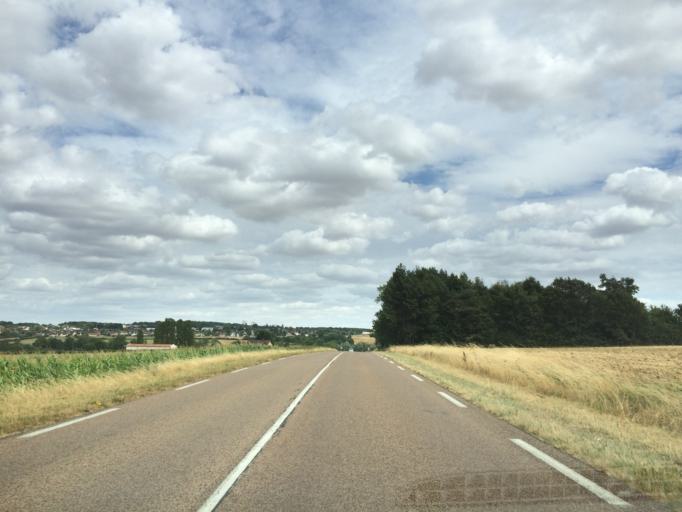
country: FR
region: Bourgogne
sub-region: Departement de l'Yonne
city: Saint-Georges-sur-Baulche
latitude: 47.8022
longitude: 3.5049
